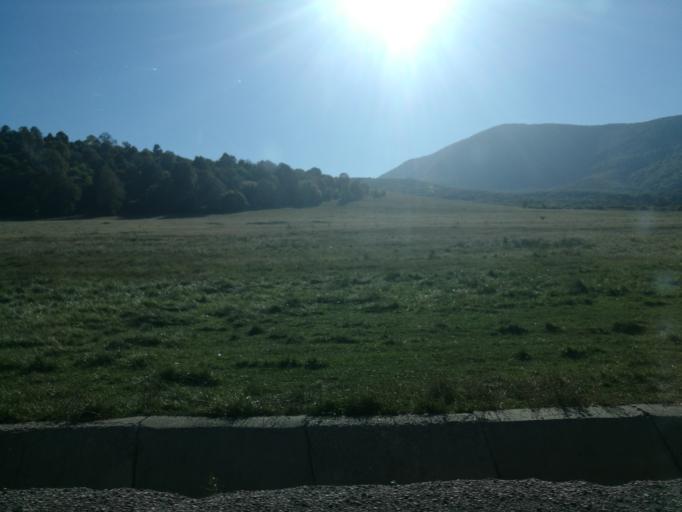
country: RO
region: Brasov
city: Codlea
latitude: 45.7294
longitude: 25.4465
